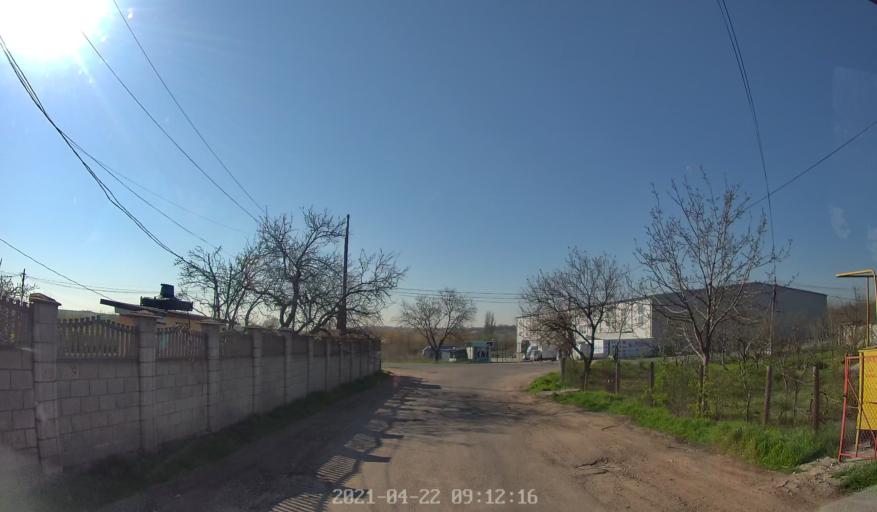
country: MD
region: Chisinau
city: Ciorescu
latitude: 47.1195
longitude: 28.8726
